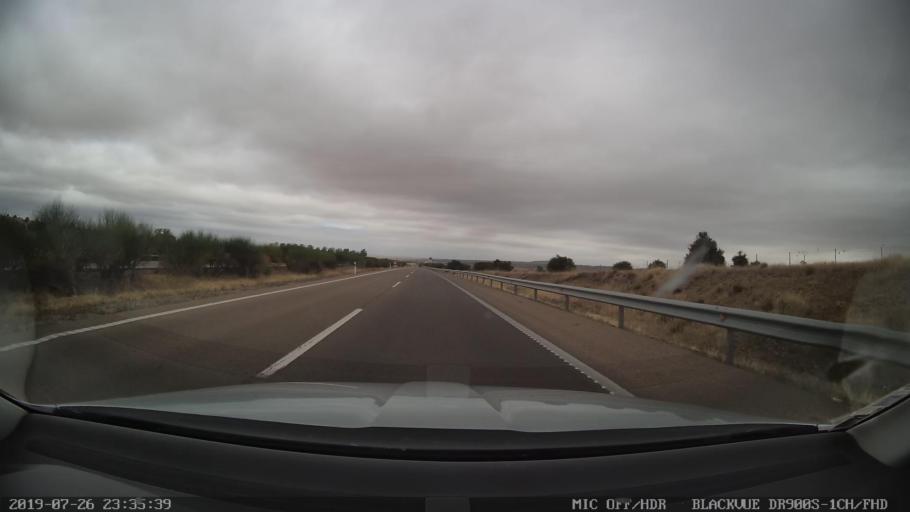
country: ES
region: Extremadura
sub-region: Provincia de Caceres
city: Santa Cruz de la Sierra
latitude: 39.3796
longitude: -5.8810
